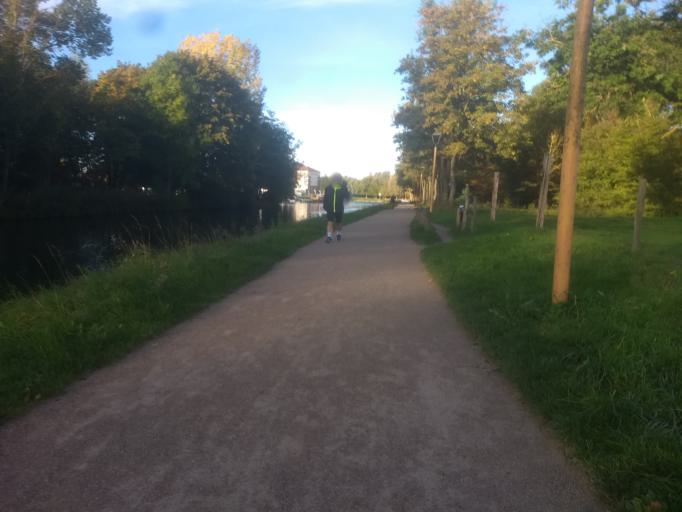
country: FR
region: Nord-Pas-de-Calais
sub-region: Departement du Pas-de-Calais
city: Saint-Laurent-Blangy
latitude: 50.2988
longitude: 2.8079
